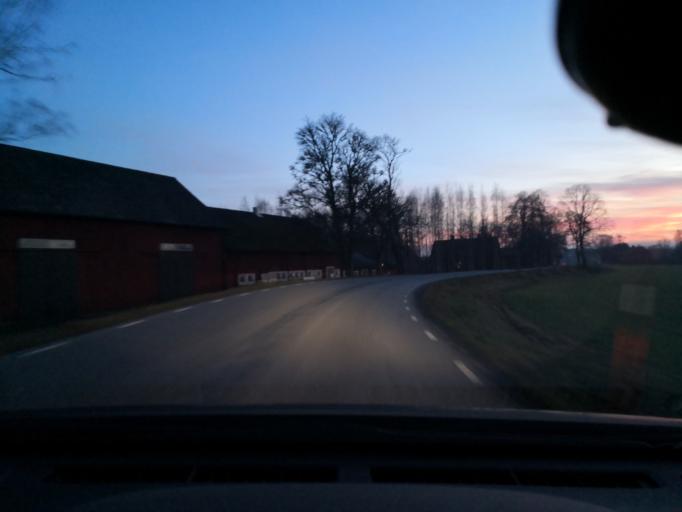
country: SE
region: OErebro
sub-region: Lindesbergs Kommun
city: Frovi
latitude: 59.3479
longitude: 15.3954
